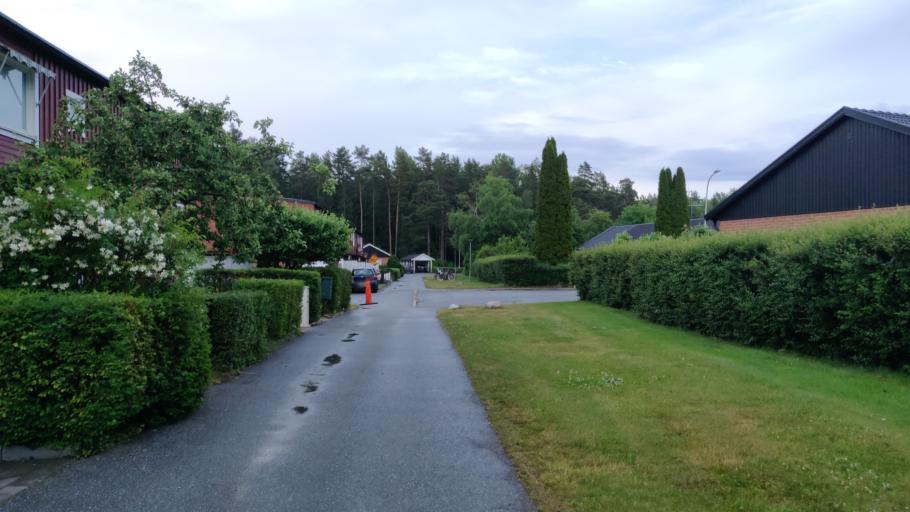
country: SE
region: OErebro
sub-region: Orebro Kommun
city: Orebro
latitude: 59.2979
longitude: 15.1701
